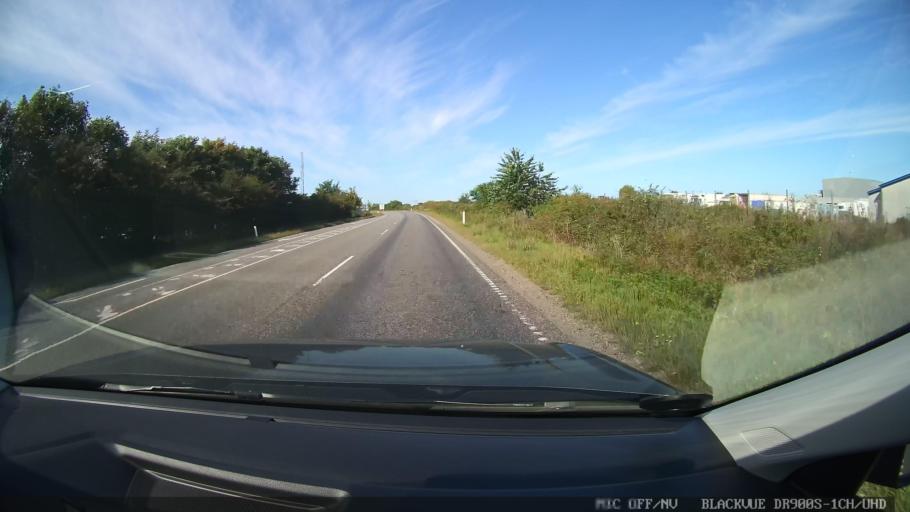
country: DK
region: North Denmark
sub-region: Mariagerfjord Kommune
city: Hobro
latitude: 56.6572
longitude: 9.8096
